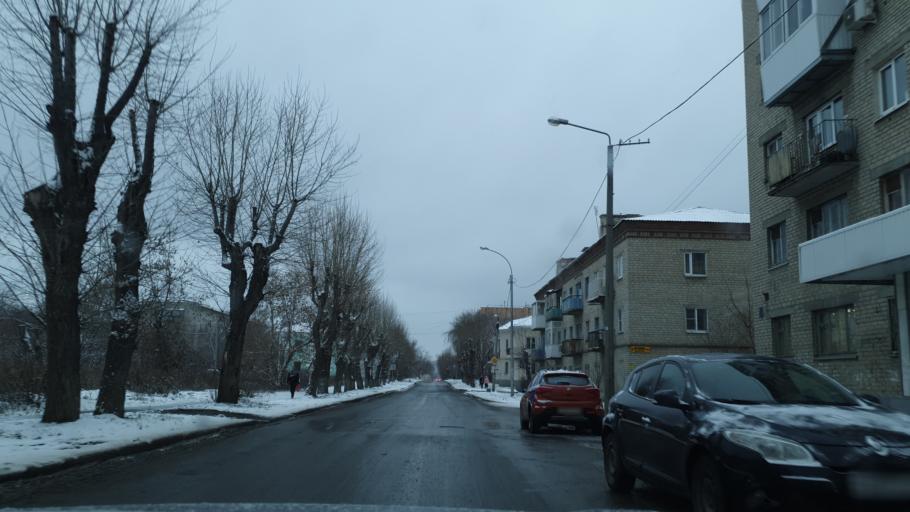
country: RU
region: Sverdlovsk
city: Istok
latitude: 56.7504
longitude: 60.7093
